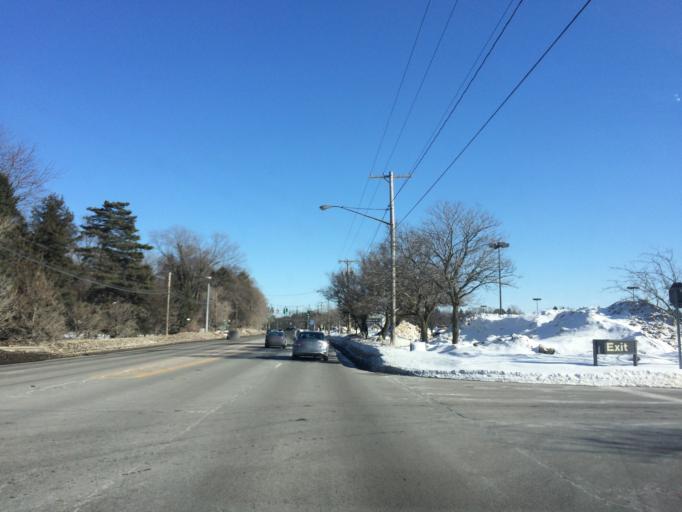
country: US
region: New York
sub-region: Monroe County
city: East Rochester
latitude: 43.1036
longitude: -77.4846
